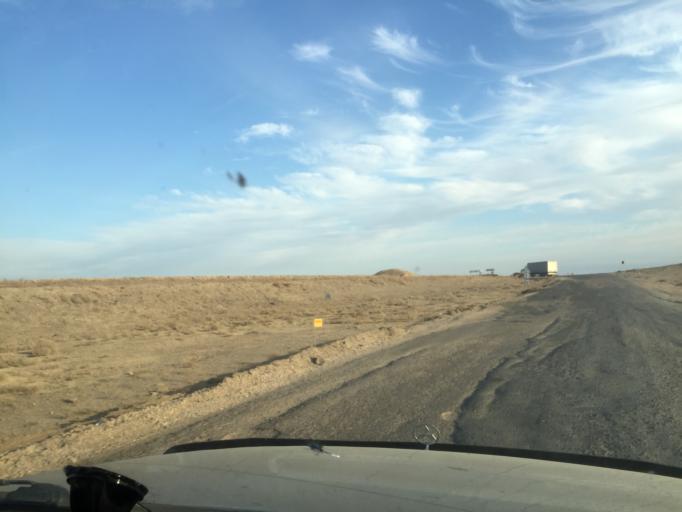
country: KZ
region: Almaty Oblysy
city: Ulken
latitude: 45.2429
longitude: 73.8233
